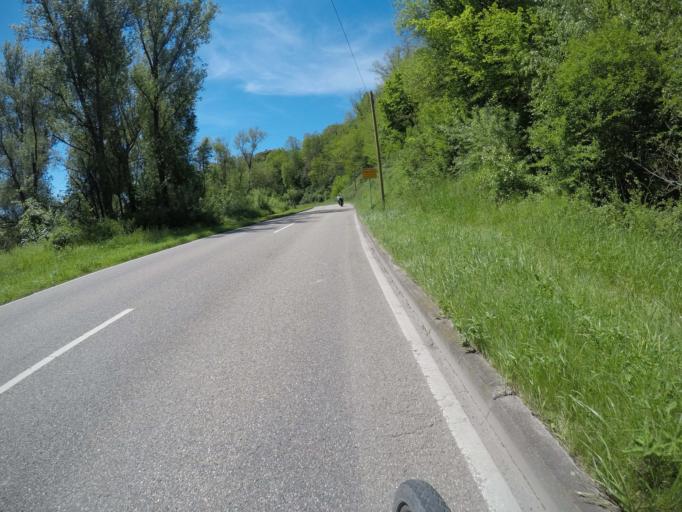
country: DE
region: Baden-Wuerttemberg
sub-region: Karlsruhe Region
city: Heimsheim
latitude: 48.7943
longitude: 8.8335
